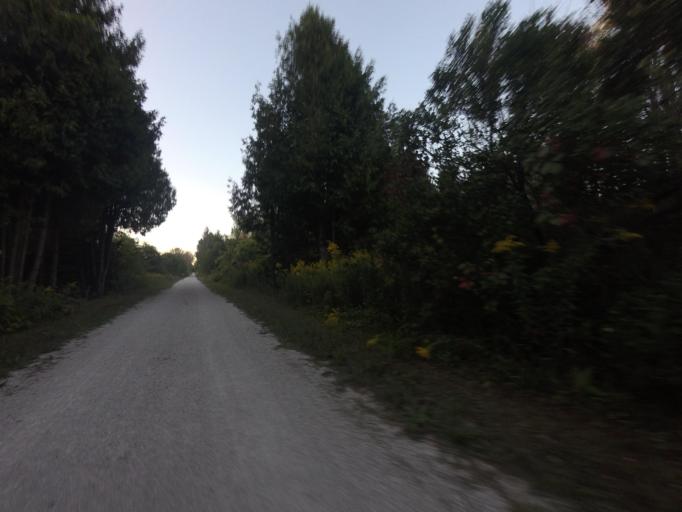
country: CA
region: Ontario
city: Brampton
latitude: 43.9260
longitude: -79.8429
